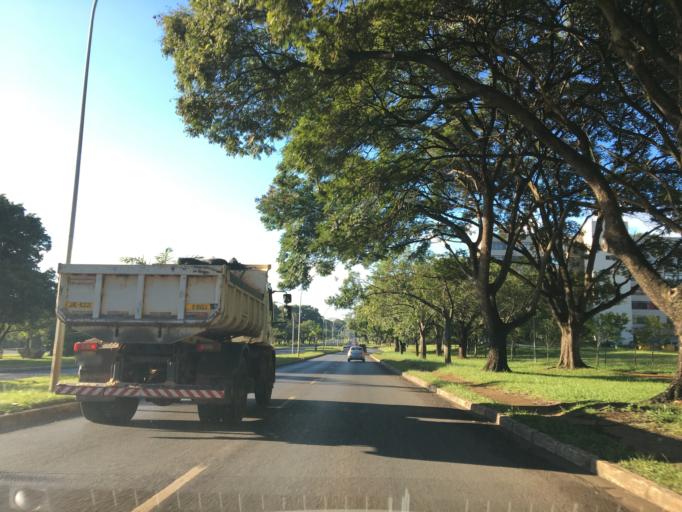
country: BR
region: Federal District
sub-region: Brasilia
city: Brasilia
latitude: -15.7473
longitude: -47.8896
